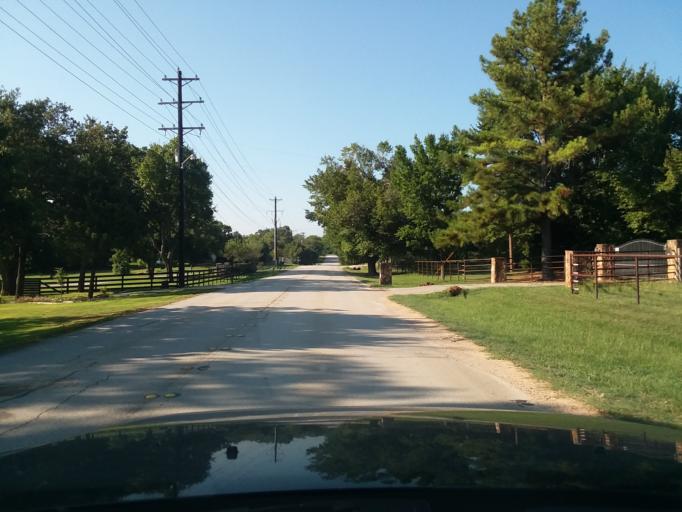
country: US
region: Texas
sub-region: Denton County
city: Copper Canyon
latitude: 33.1001
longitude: -97.0879
